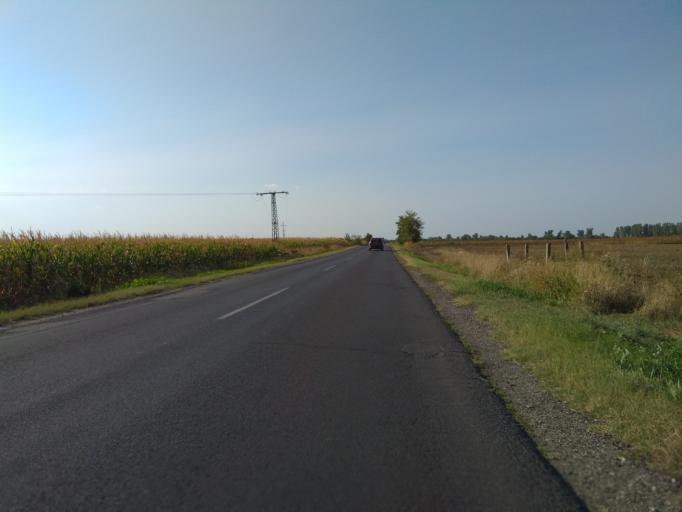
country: HU
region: Borsod-Abauj-Zemplen
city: Onod
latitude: 48.0153
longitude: 20.9074
